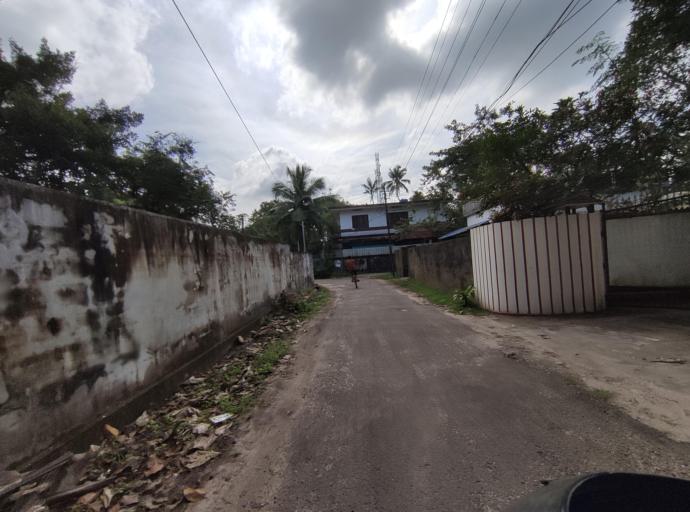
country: IN
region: Kerala
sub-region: Alappuzha
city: Vayalar
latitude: 9.6899
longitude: 76.3314
